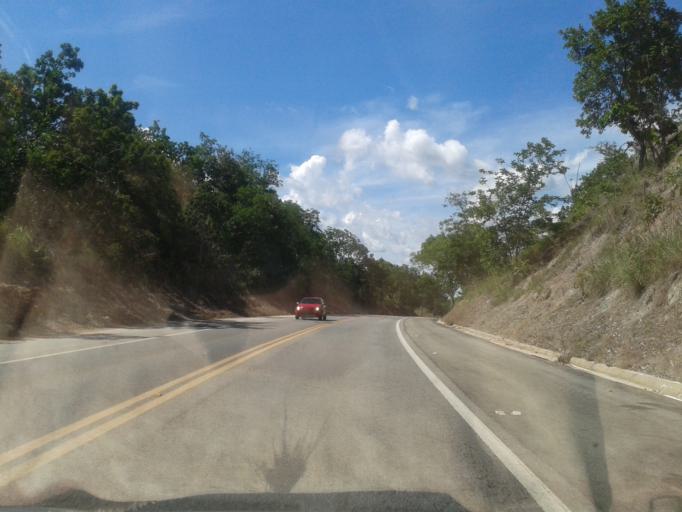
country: BR
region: Goias
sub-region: Goias
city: Goias
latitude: -15.6688
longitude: -50.2153
